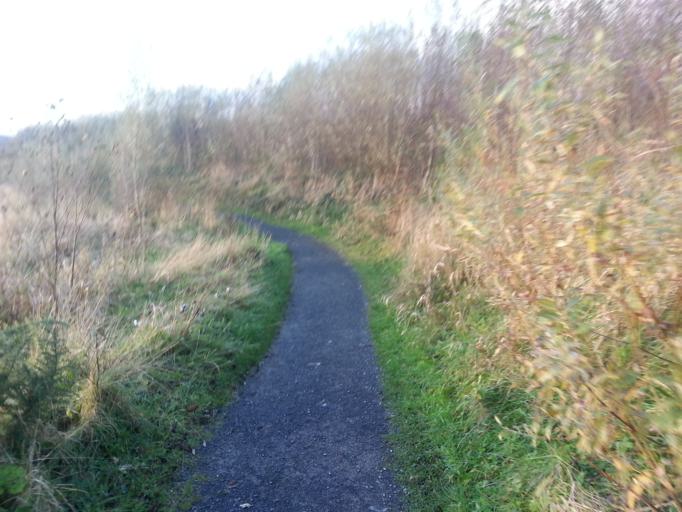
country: IE
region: Ulster
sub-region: County Monaghan
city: Clones
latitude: 54.2278
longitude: -7.2792
